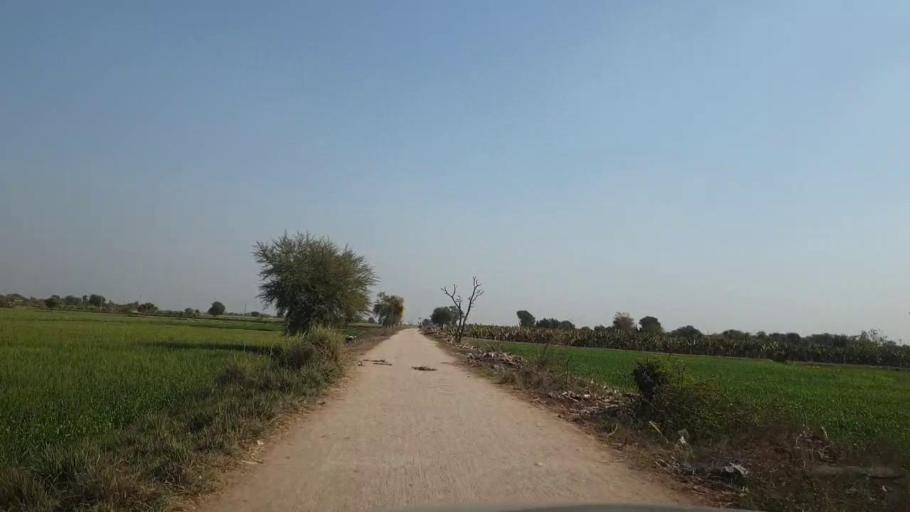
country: PK
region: Sindh
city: Tando Allahyar
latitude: 25.5870
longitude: 68.7498
